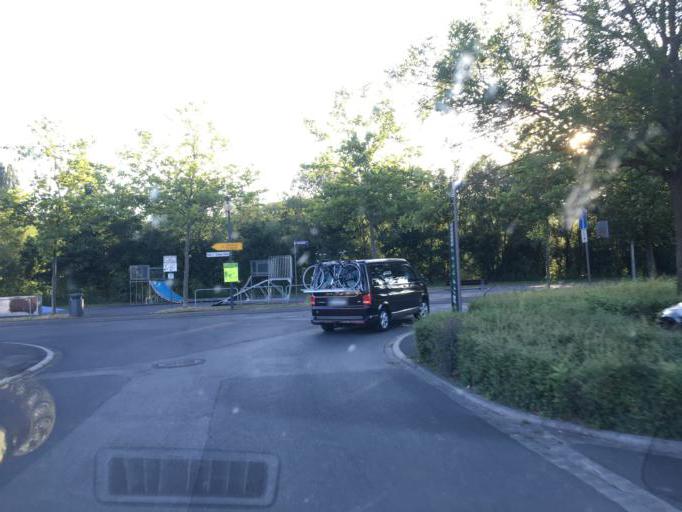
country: DE
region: Bavaria
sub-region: Regierungsbezirk Unterfranken
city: Margetshochheim
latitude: 49.8297
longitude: 9.8701
